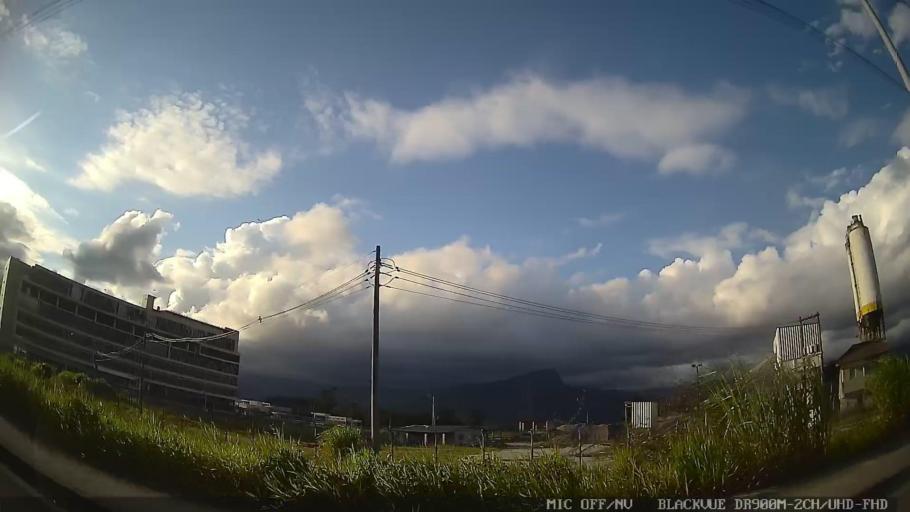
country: BR
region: Sao Paulo
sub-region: Caraguatatuba
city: Caraguatatuba
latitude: -23.6584
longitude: -45.4388
